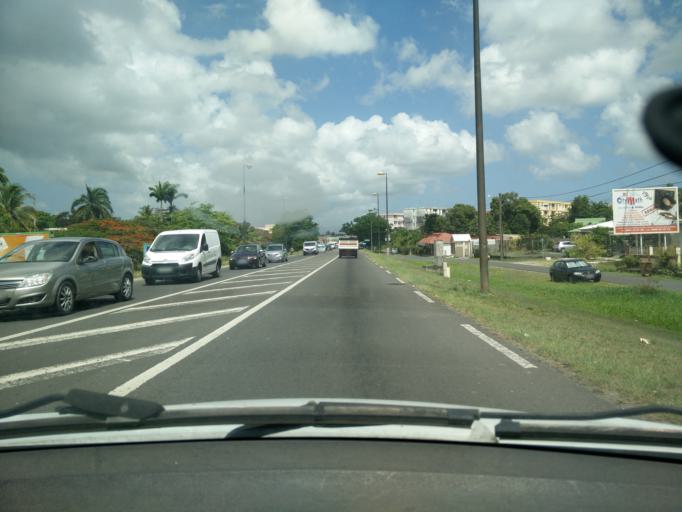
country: GP
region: Guadeloupe
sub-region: Guadeloupe
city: Pointe-a-Pitre
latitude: 16.2515
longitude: -61.5168
